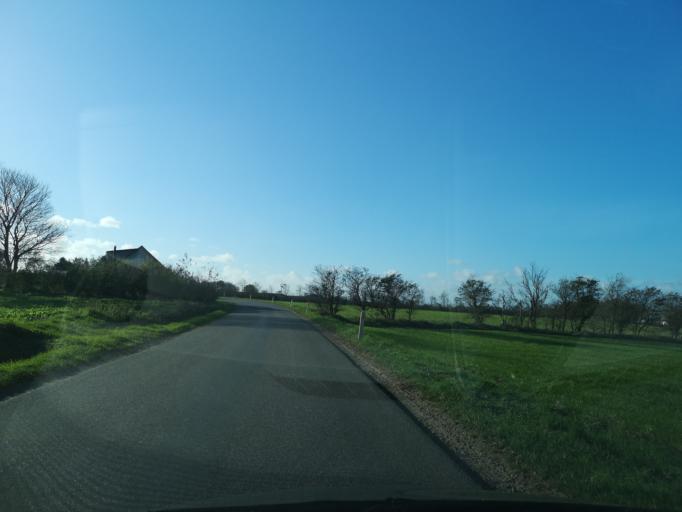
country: DK
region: Central Jutland
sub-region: Ringkobing-Skjern Kommune
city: Tarm
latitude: 55.8044
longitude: 8.4662
